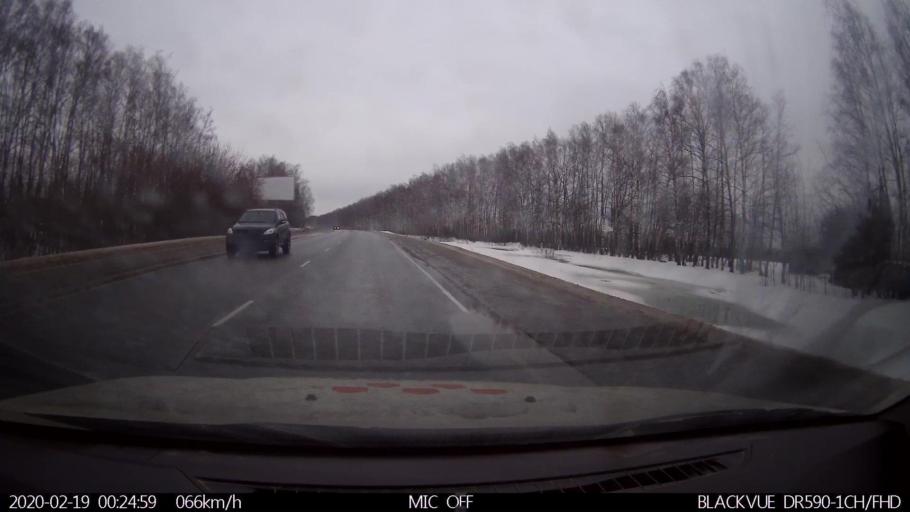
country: RU
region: Nizjnij Novgorod
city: Nizhniy Novgorod
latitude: 56.2188
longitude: 43.9427
